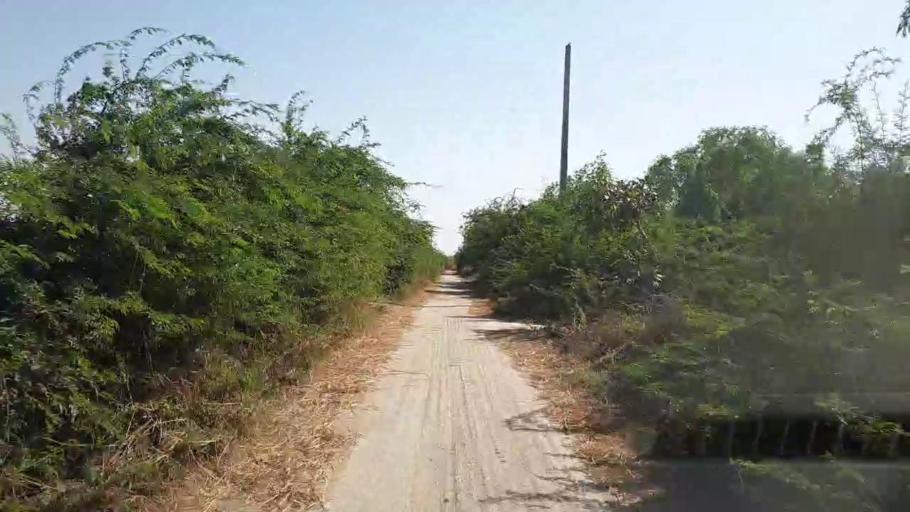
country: PK
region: Sindh
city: Tando Bago
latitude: 24.6383
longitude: 68.9908
